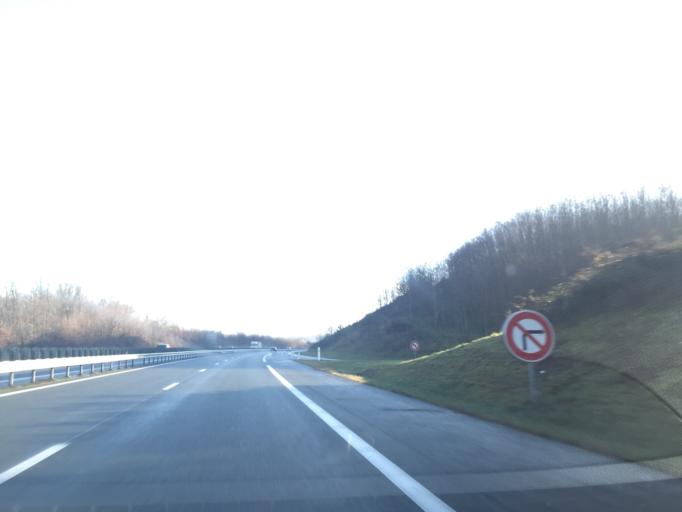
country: FR
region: Limousin
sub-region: Departement de la Correze
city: Saint-Pantaleon-de-Larche
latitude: 45.1631
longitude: 1.4425
